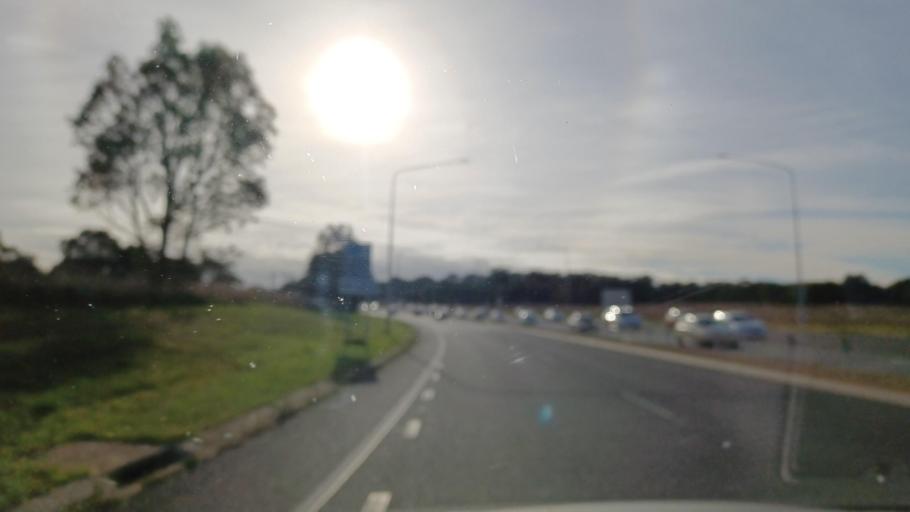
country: AU
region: Australian Capital Territory
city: Kaleen
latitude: -35.2239
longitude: 149.1261
